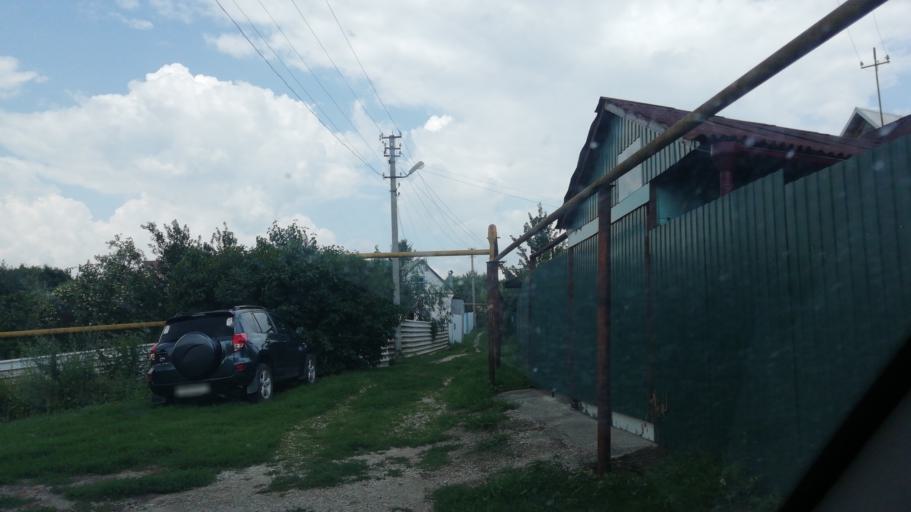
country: RU
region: Tula
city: Mendeleyevskiy
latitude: 54.1608
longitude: 37.5655
